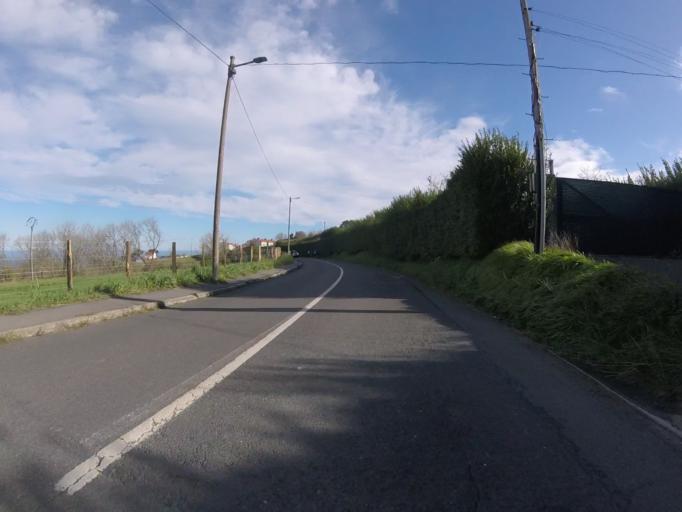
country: ES
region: Basque Country
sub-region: Provincia de Guipuzcoa
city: Usurbil
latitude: 43.3065
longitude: -2.0402
